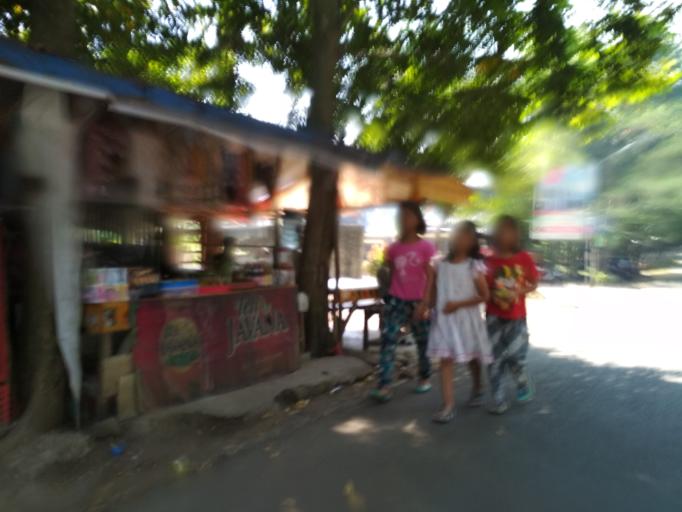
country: ID
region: West Java
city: Ciampea
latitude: -6.5579
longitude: 106.7498
